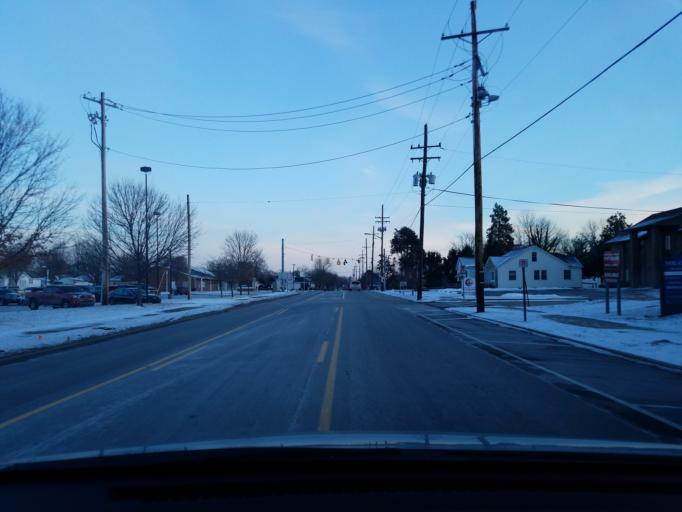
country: US
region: Indiana
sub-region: Floyd County
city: New Albany
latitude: 38.3001
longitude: -85.8347
